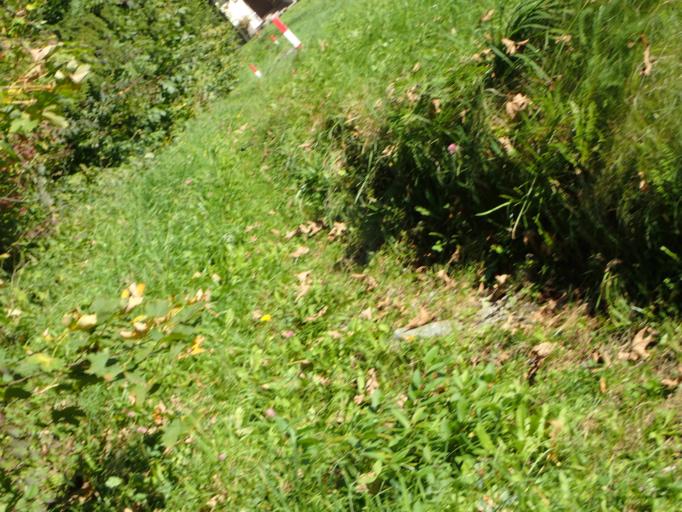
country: AT
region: Salzburg
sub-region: Politischer Bezirk Hallein
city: Oberalm
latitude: 47.6944
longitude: 13.0771
